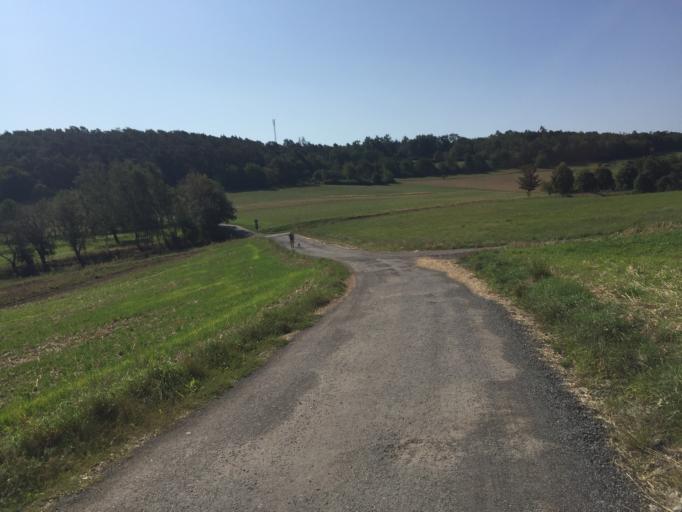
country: DE
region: Hesse
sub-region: Regierungsbezirk Giessen
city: Schoeffengrund
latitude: 50.4417
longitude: 8.5600
